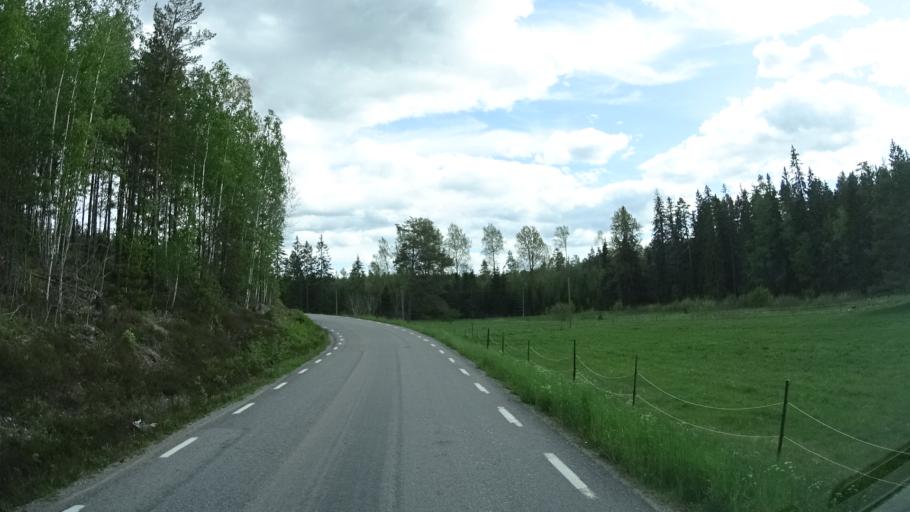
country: SE
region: OEstergoetland
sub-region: Finspangs Kommun
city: Finspang
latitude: 58.6055
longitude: 15.7490
